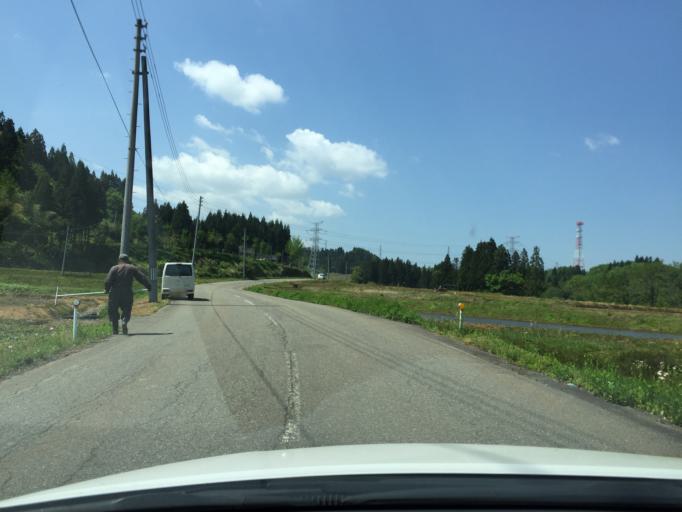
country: JP
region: Niigata
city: Tochio-honcho
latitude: 37.4861
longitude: 139.0513
